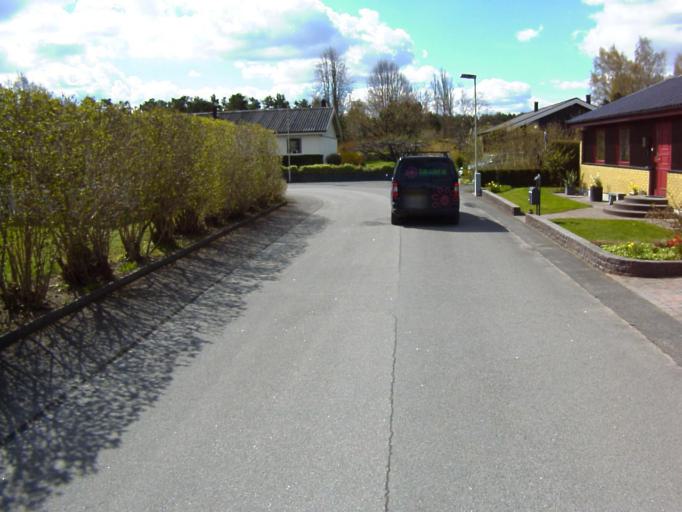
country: SE
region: Skane
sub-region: Kristianstads Kommun
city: Norra Asum
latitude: 56.0072
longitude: 14.0964
